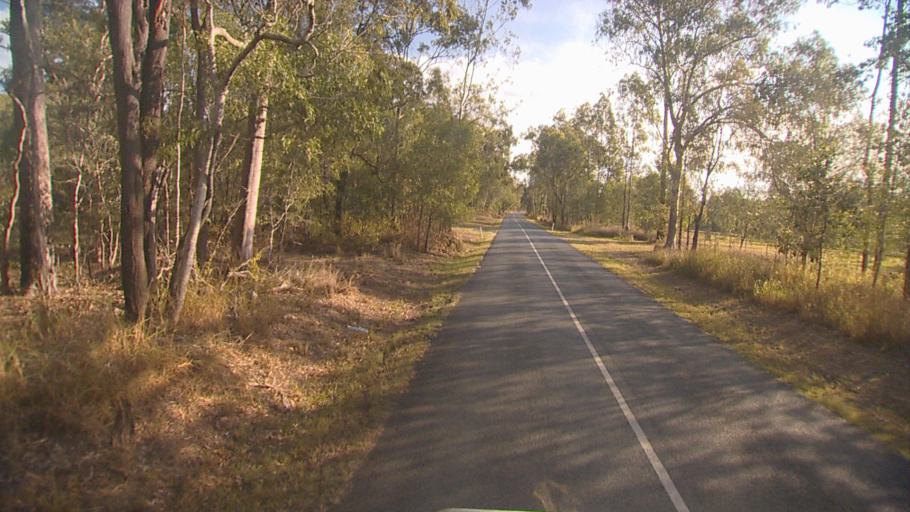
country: AU
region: Queensland
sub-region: Logan
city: Cedar Vale
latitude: -27.8517
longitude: 153.1296
